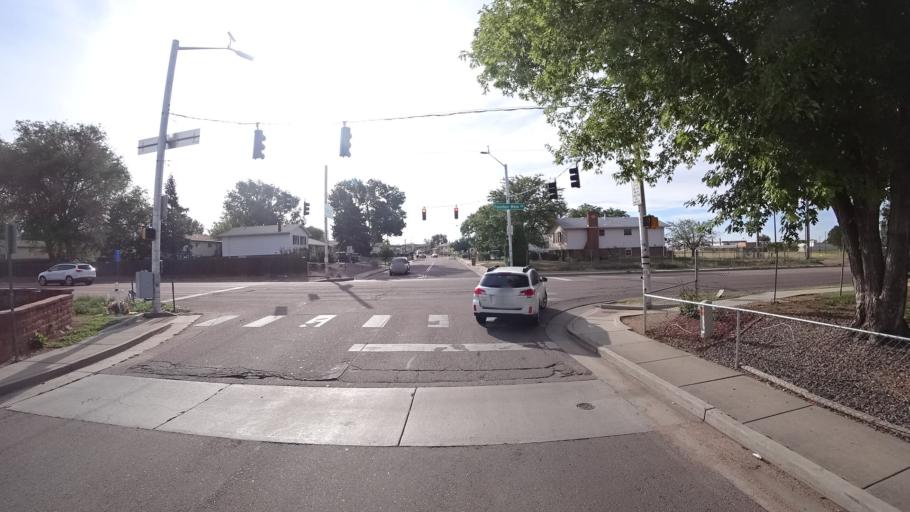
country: US
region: Colorado
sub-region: El Paso County
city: Security-Widefield
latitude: 38.7234
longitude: -104.6997
